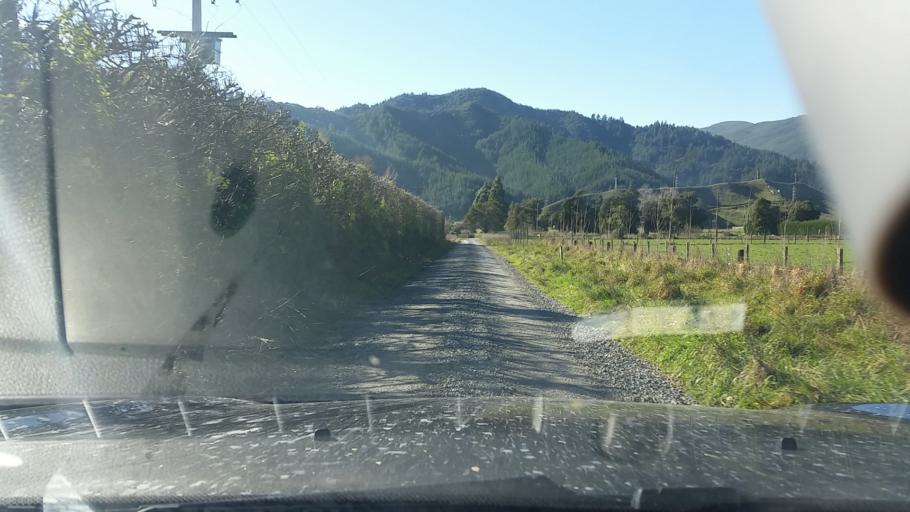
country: NZ
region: Marlborough
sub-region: Marlborough District
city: Blenheim
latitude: -41.4317
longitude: 173.7623
